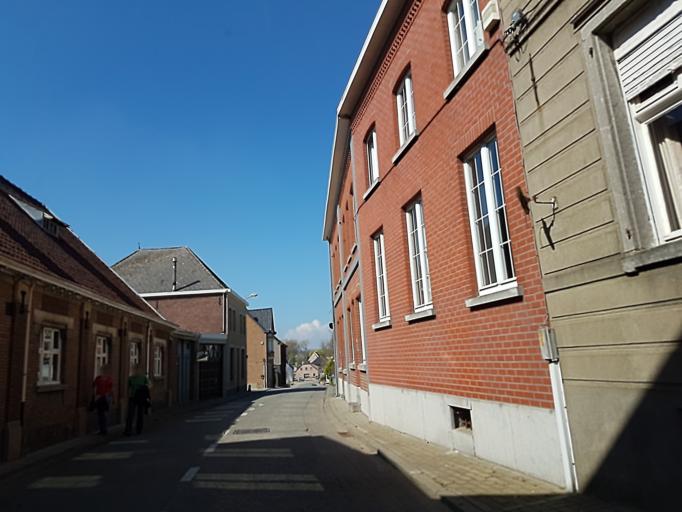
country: BE
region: Flanders
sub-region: Provincie Oost-Vlaanderen
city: Sint-Maria-Lierde
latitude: 50.8217
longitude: 3.8464
